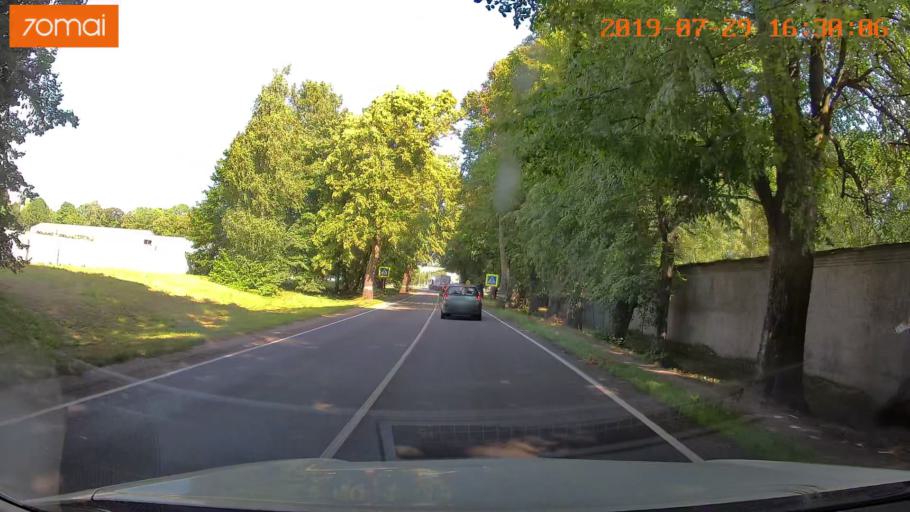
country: RU
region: Kaliningrad
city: Primorsk
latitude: 54.7297
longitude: 19.9960
